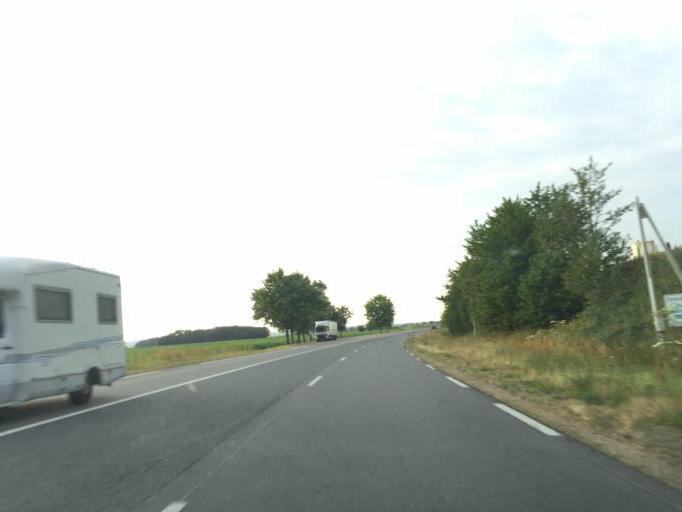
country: FR
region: Auvergne
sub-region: Departement de l'Allier
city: Varennes-sur-Allier
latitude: 46.3685
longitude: 3.3649
